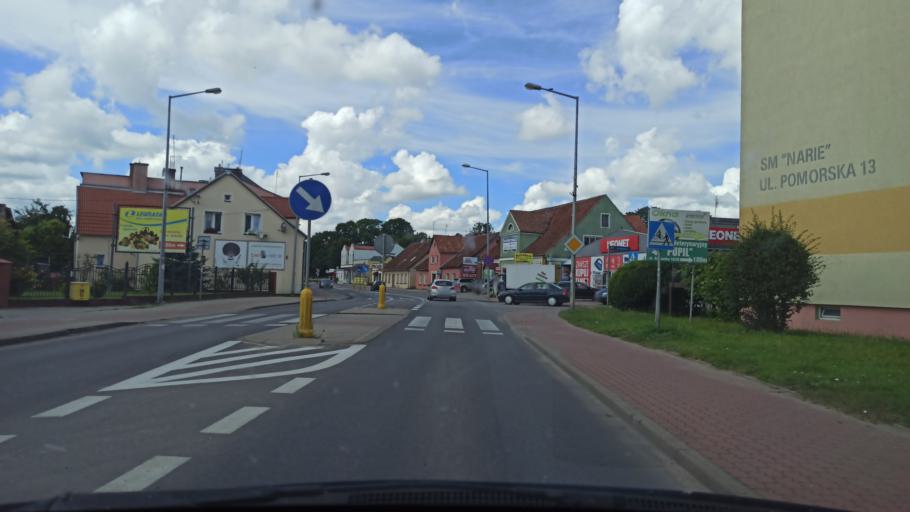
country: PL
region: Warmian-Masurian Voivodeship
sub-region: Powiat ostrodzki
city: Morag
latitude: 53.9104
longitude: 19.9328
